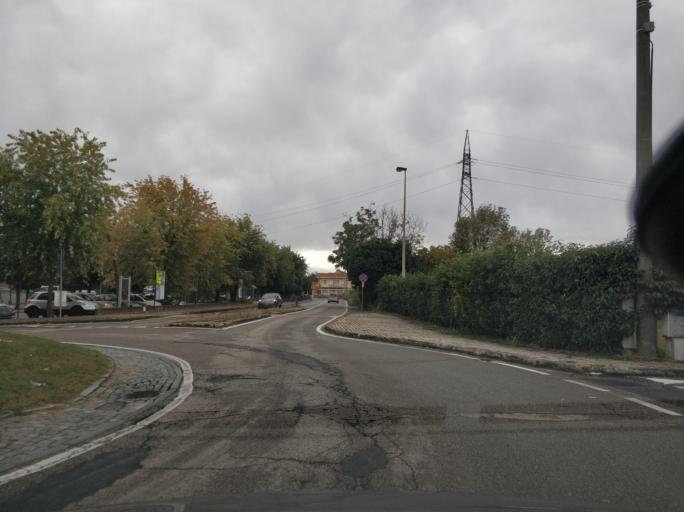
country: IT
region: Piedmont
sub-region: Provincia di Torino
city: Cirie
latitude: 45.2217
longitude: 7.5989
